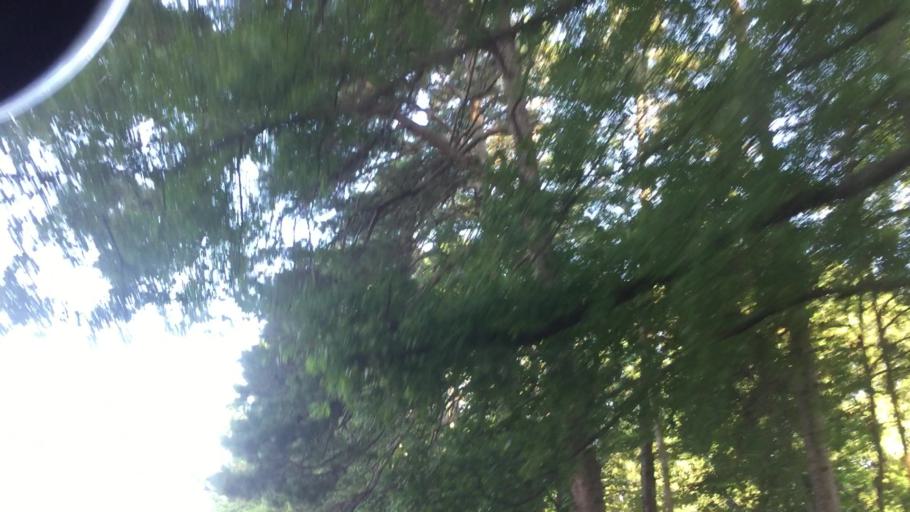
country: US
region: Georgia
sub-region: DeKalb County
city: Panthersville
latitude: 33.7087
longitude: -84.2148
